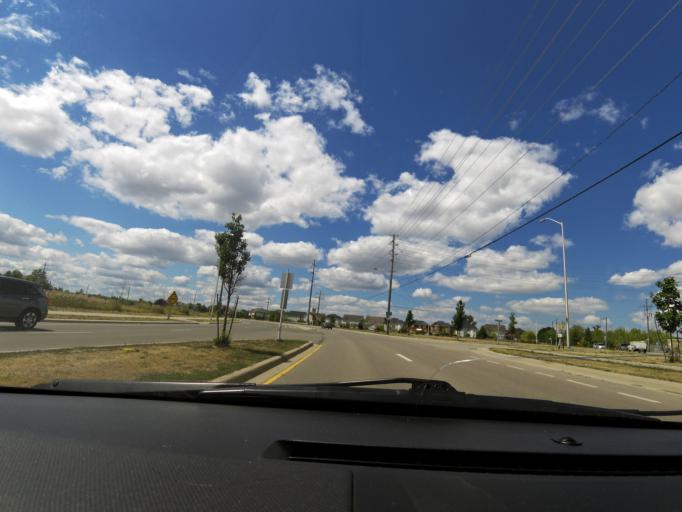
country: CA
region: Ontario
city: Burlington
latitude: 43.4073
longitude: -79.7732
